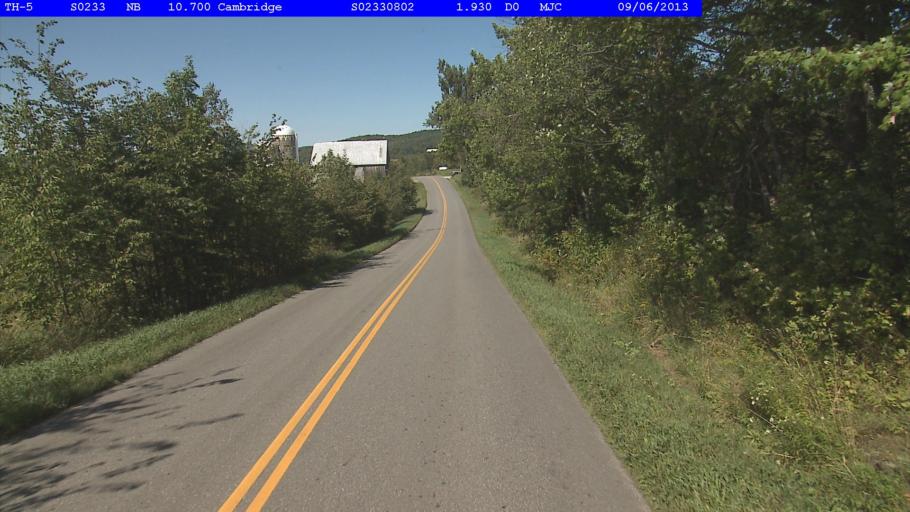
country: US
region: Vermont
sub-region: Chittenden County
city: Jericho
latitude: 44.6096
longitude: -72.8565
